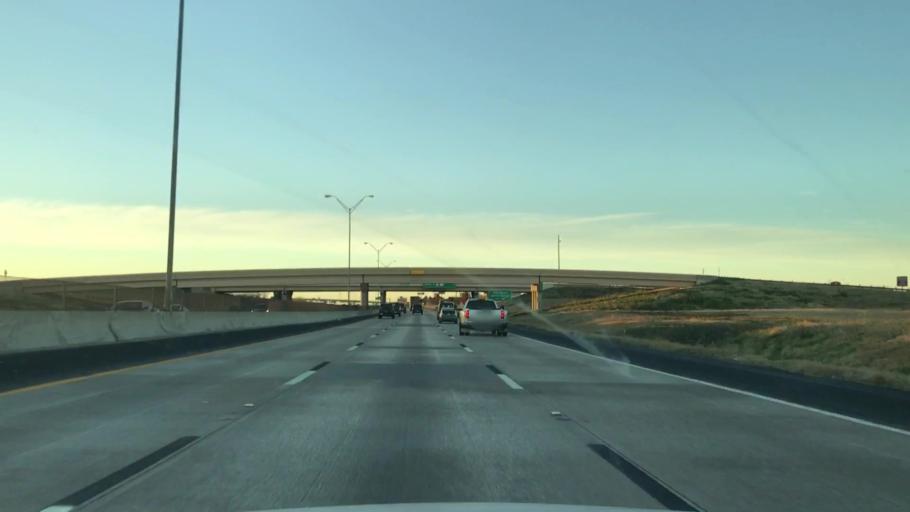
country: US
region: Texas
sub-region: Johnson County
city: Burleson
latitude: 32.5798
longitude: -97.3197
